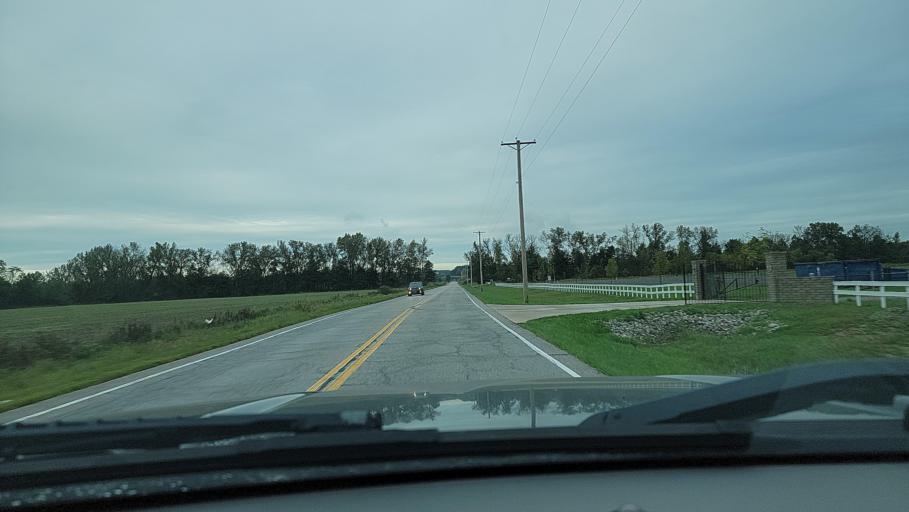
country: US
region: Indiana
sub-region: Porter County
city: Portage
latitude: 41.5653
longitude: -87.1533
